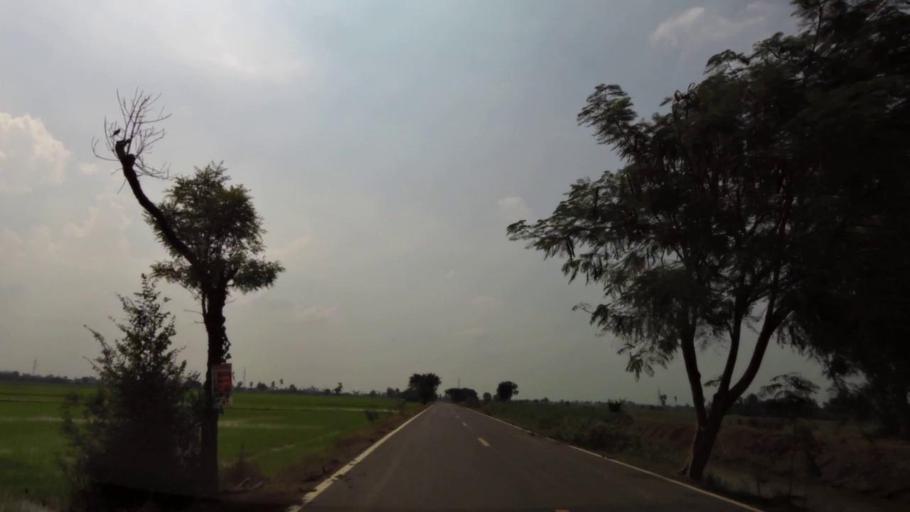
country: TH
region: Ang Thong
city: Pho Thong
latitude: 14.6267
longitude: 100.4051
